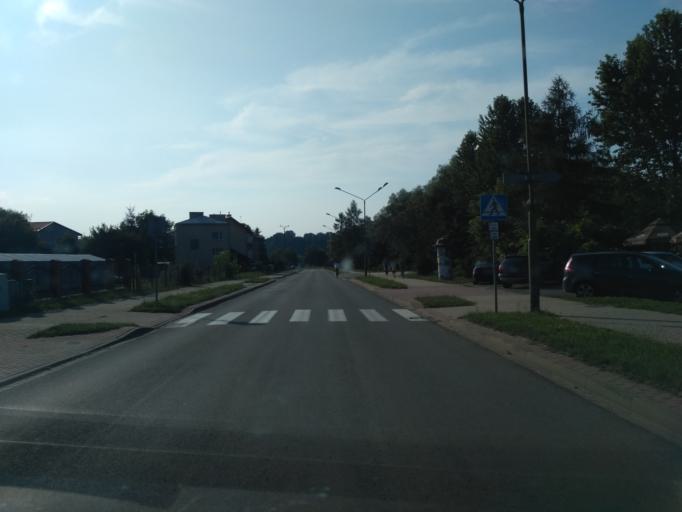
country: PL
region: Subcarpathian Voivodeship
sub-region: Powiat sanocki
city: Sanok
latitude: 49.5731
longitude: 22.2035
